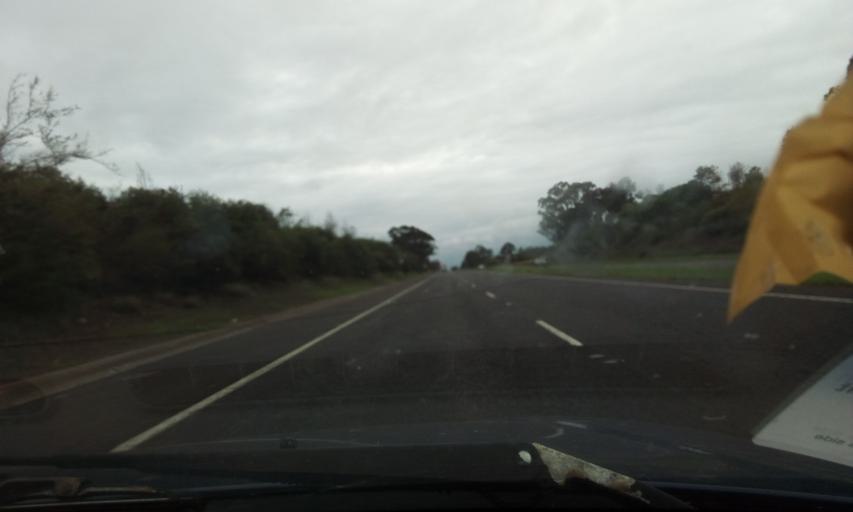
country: AU
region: New South Wales
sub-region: Camden
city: Narellan Vale
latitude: -34.0582
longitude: 150.7310
